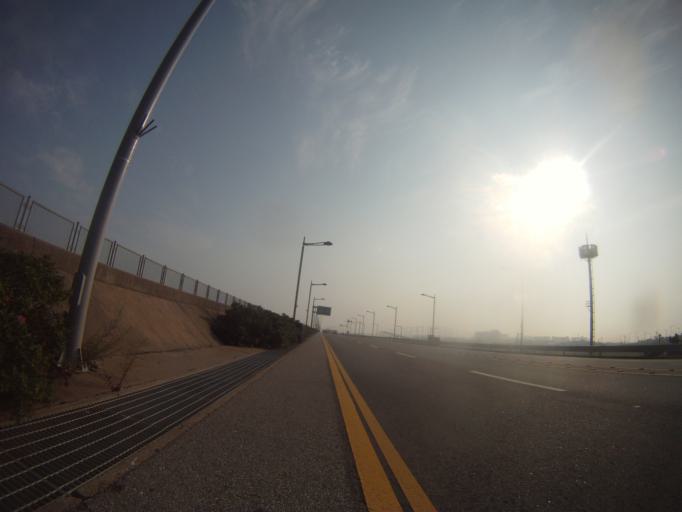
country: KR
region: Incheon
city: Incheon
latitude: 37.4353
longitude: 126.4672
